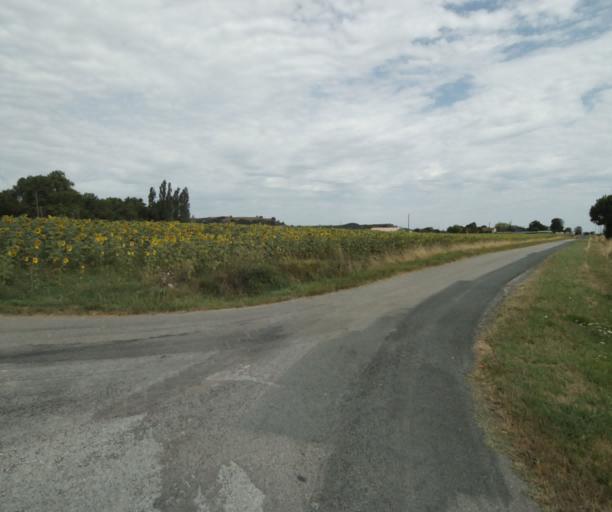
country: FR
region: Midi-Pyrenees
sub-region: Departement de la Haute-Garonne
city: Saint-Felix-Lauragais
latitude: 43.4278
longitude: 1.8994
